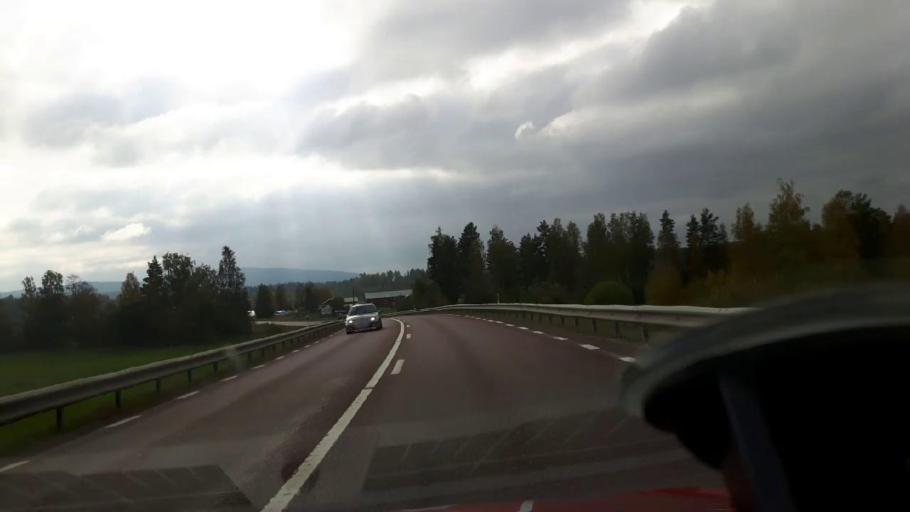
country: SE
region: Gaevleborg
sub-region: Bollnas Kommun
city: Kilafors
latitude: 61.2472
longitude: 16.5497
